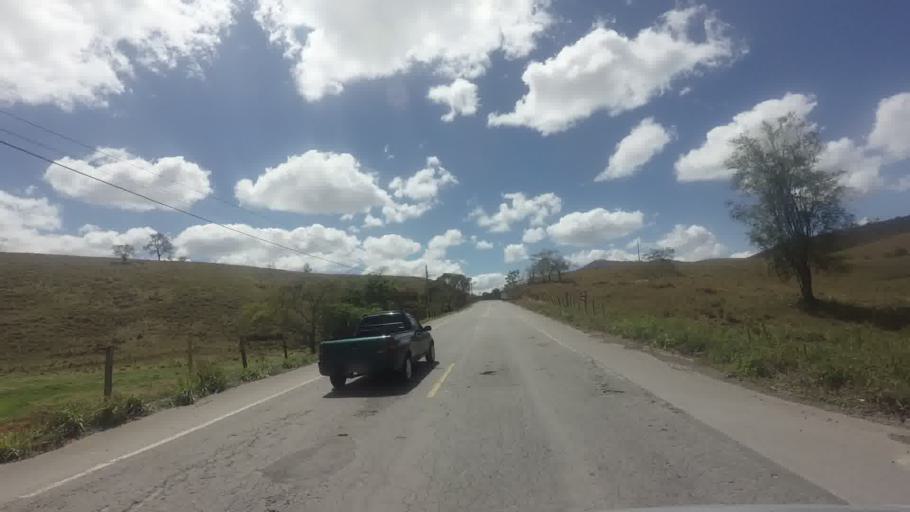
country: BR
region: Rio de Janeiro
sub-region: Santo Antonio De Padua
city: Santo Antonio de Padua
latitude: -21.6485
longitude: -42.2886
